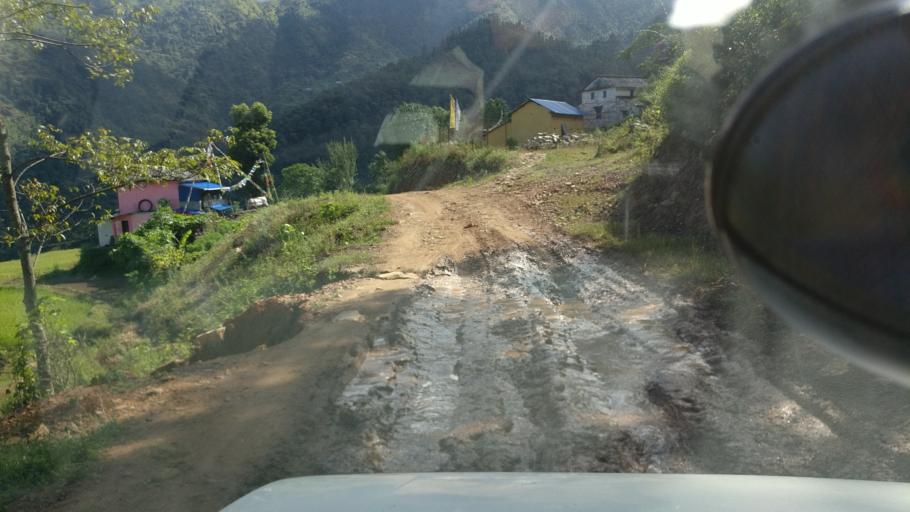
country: NP
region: Western Region
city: Waling
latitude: 28.1209
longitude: 83.6729
